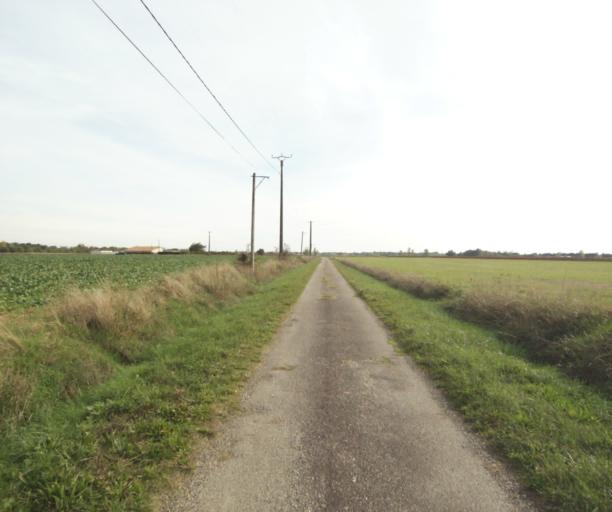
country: FR
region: Midi-Pyrenees
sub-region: Departement du Tarn-et-Garonne
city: Bressols
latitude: 43.9343
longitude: 1.3344
